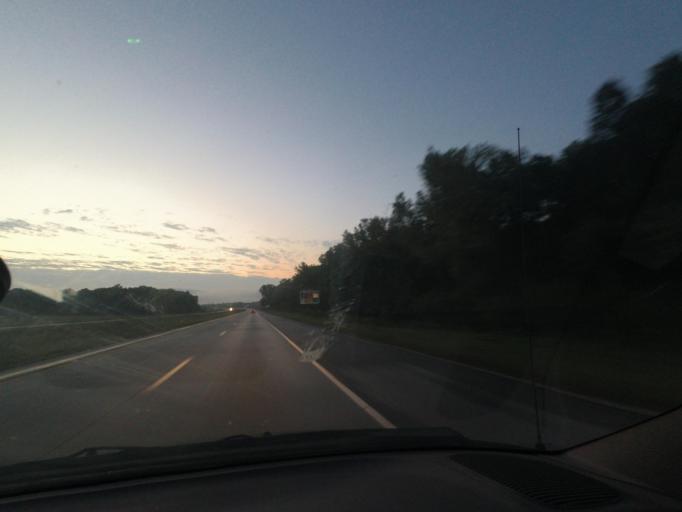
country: US
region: Missouri
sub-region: Linn County
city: Brookfield
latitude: 39.7746
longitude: -93.0865
